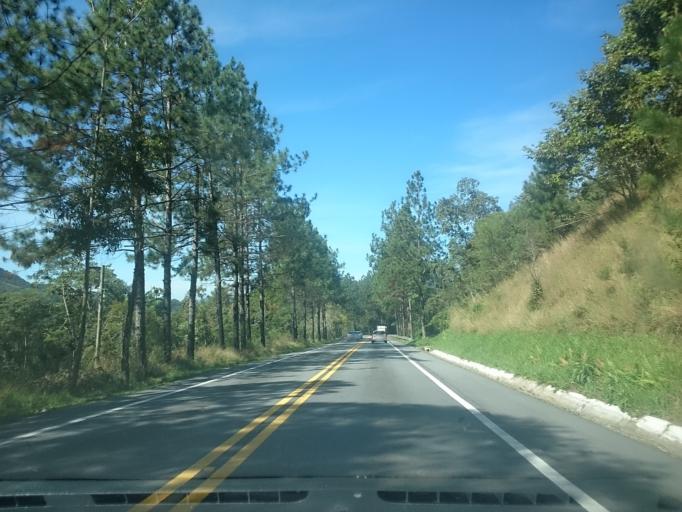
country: BR
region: Santa Catarina
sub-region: Santo Amaro Da Imperatriz
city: Santo Amaro da Imperatriz
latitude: -27.7105
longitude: -48.9477
